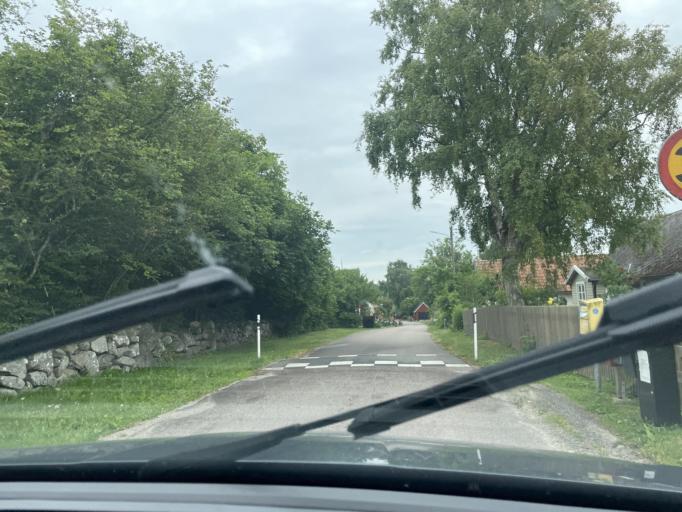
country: SE
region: Skane
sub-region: Bromolla Kommun
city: Bromoella
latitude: 56.0099
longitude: 14.4350
